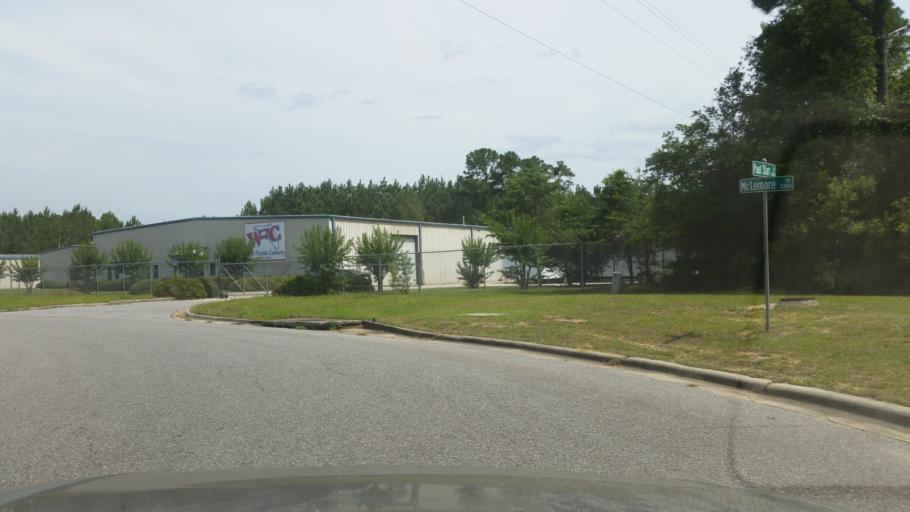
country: US
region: Florida
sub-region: Escambia County
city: Ferry Pass
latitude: 30.5204
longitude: -87.1979
